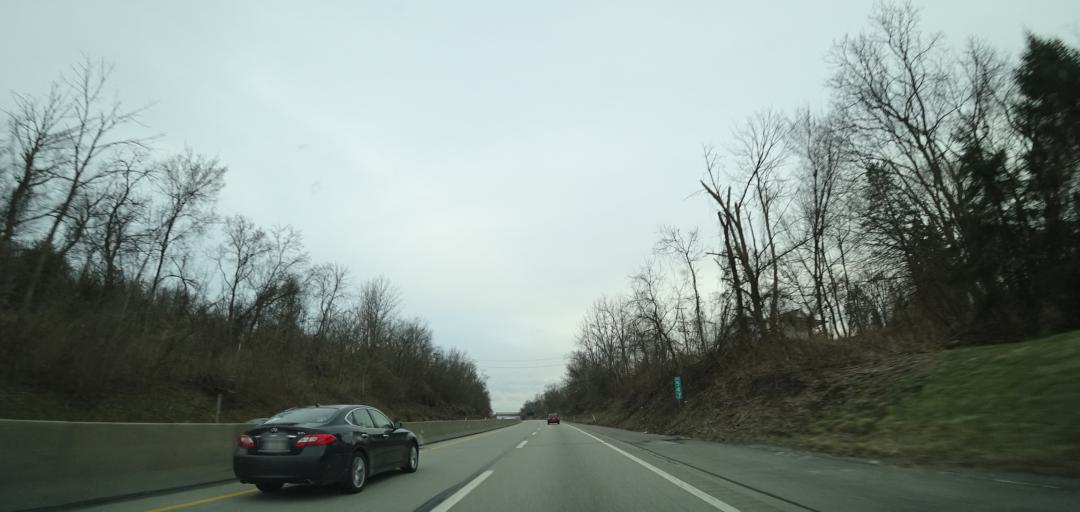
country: US
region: Pennsylvania
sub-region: Allegheny County
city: Plum
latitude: 40.4616
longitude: -79.7604
